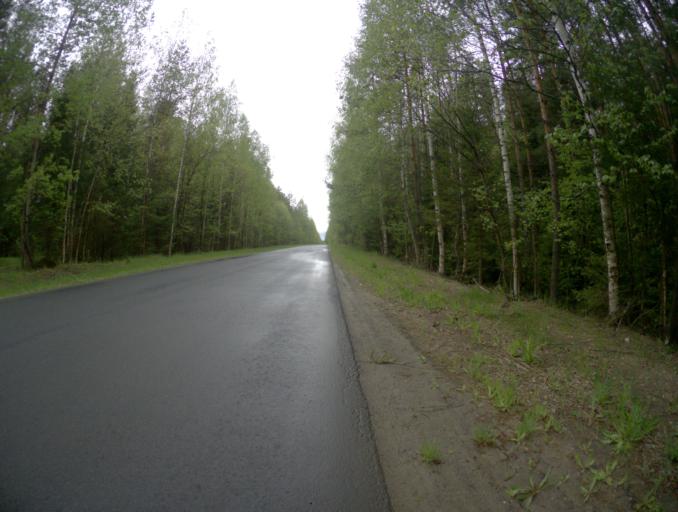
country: RU
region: Vladimir
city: Zolotkovo
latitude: 55.3457
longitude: 40.9811
